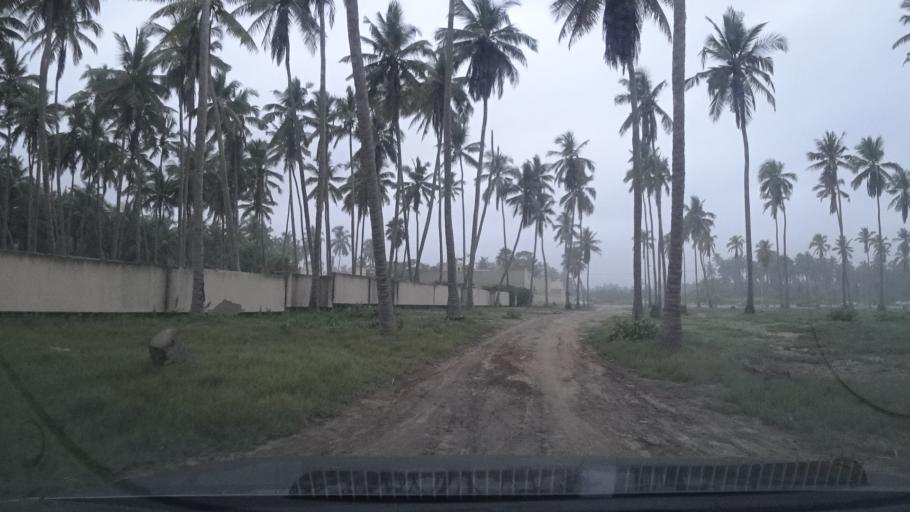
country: OM
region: Zufar
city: Salalah
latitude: 17.0029
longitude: 54.1188
